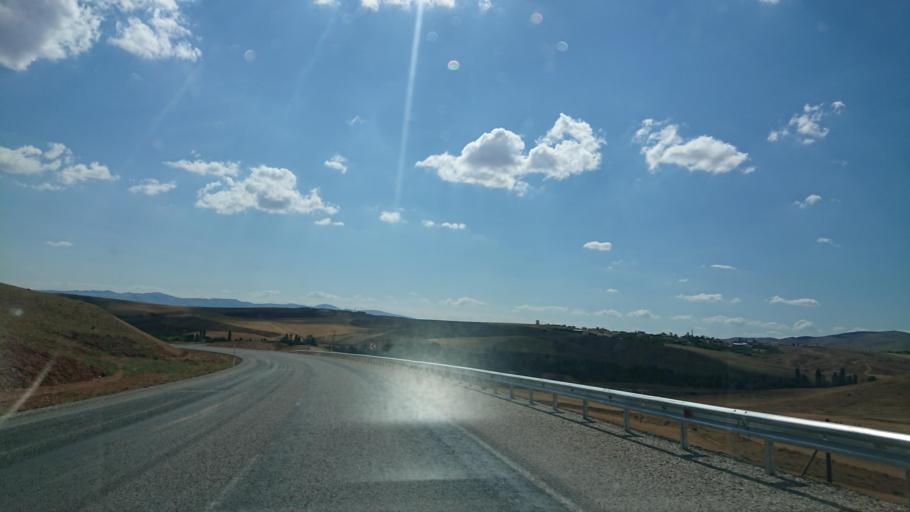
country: TR
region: Ankara
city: Evren
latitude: 39.1069
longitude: 33.9155
